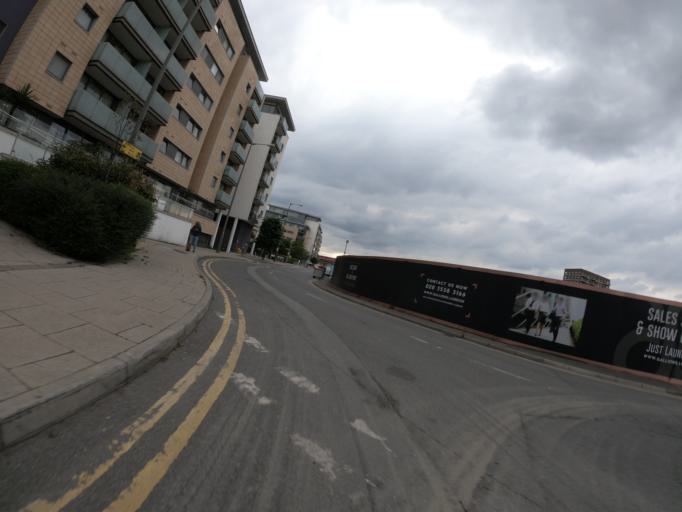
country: GB
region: England
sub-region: Greater London
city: Woolwich
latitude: 51.5073
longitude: 0.0744
